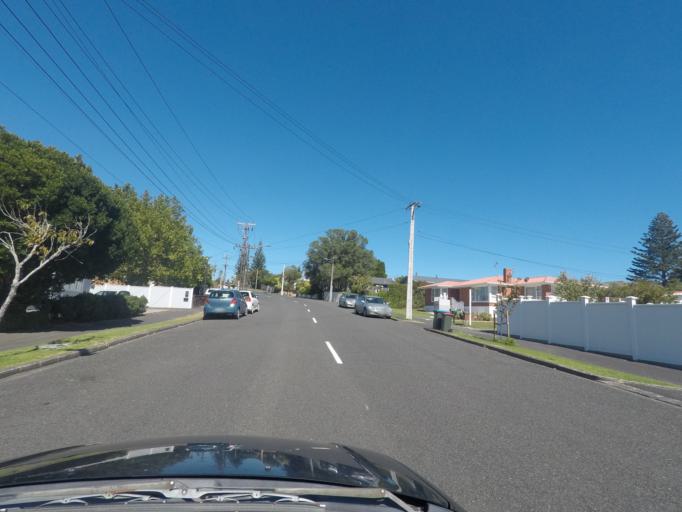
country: NZ
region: Auckland
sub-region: Auckland
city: Rosebank
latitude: -36.8979
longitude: 174.7055
